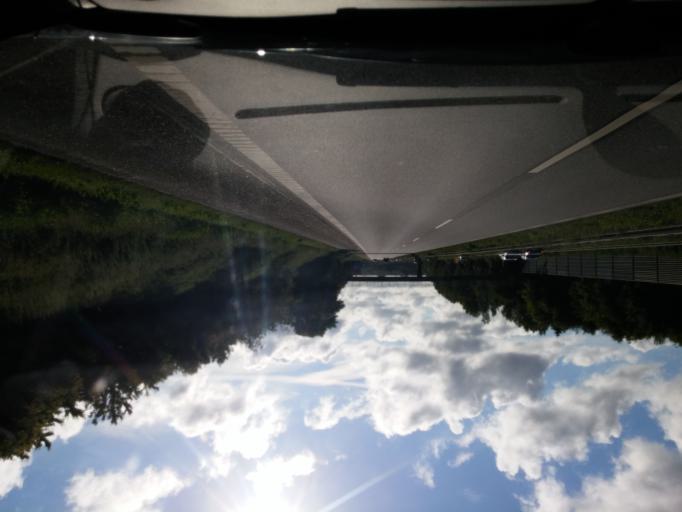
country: DK
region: Zealand
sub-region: Slagelse Kommune
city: Slagelse
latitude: 55.3872
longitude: 11.3504
